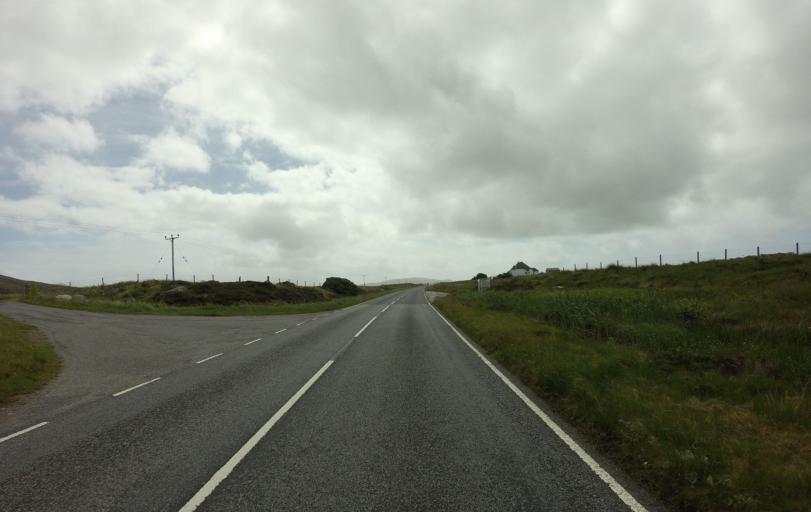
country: GB
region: Scotland
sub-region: Eilean Siar
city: Isle of South Uist
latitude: 57.1848
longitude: -7.3832
